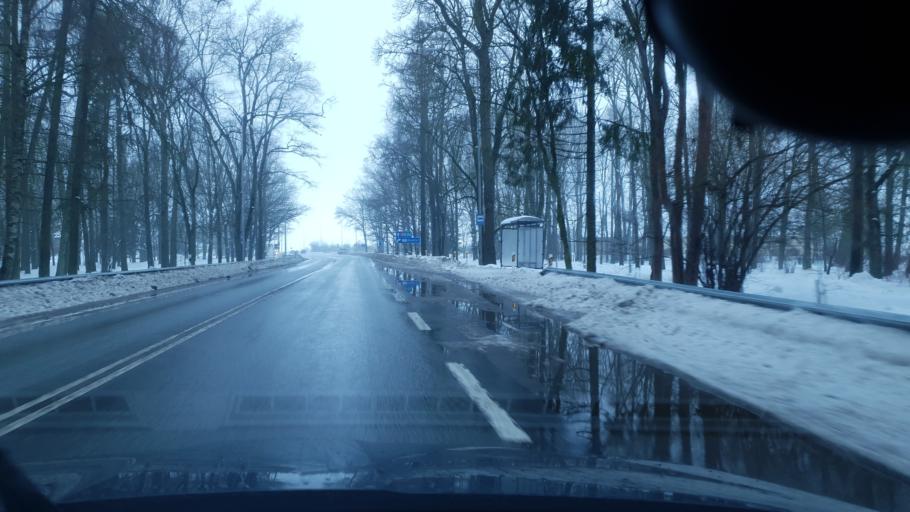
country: EE
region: Jogevamaa
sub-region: Poltsamaa linn
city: Poltsamaa
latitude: 58.7079
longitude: 25.8977
